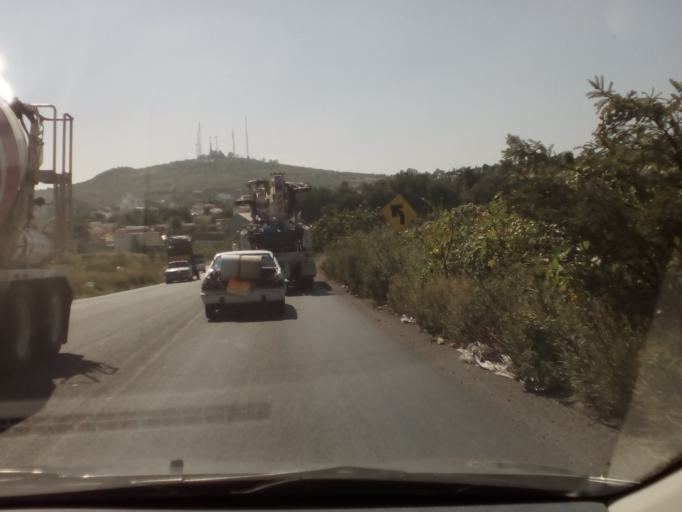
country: MX
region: Guanajuato
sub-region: Leon
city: La Ermita
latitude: 21.1740
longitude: -101.7224
